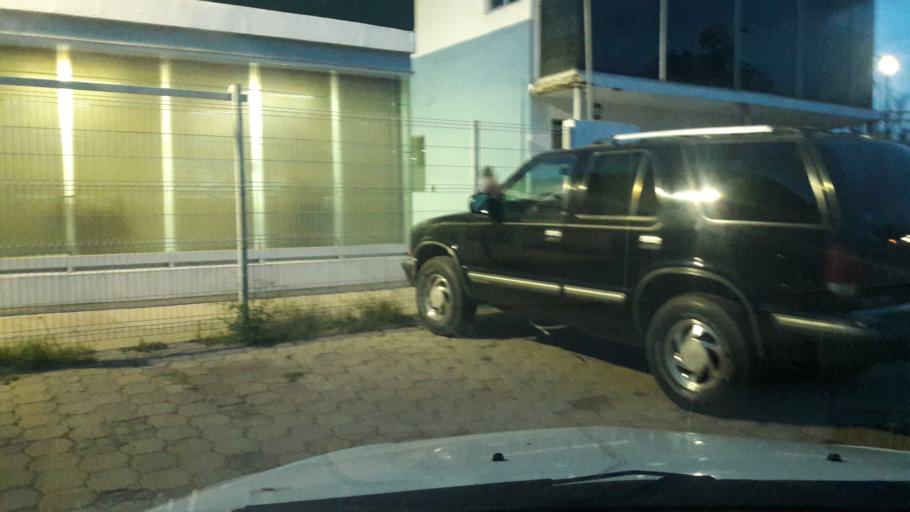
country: MX
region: Guanajuato
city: Leon
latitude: 21.1058
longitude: -101.6410
